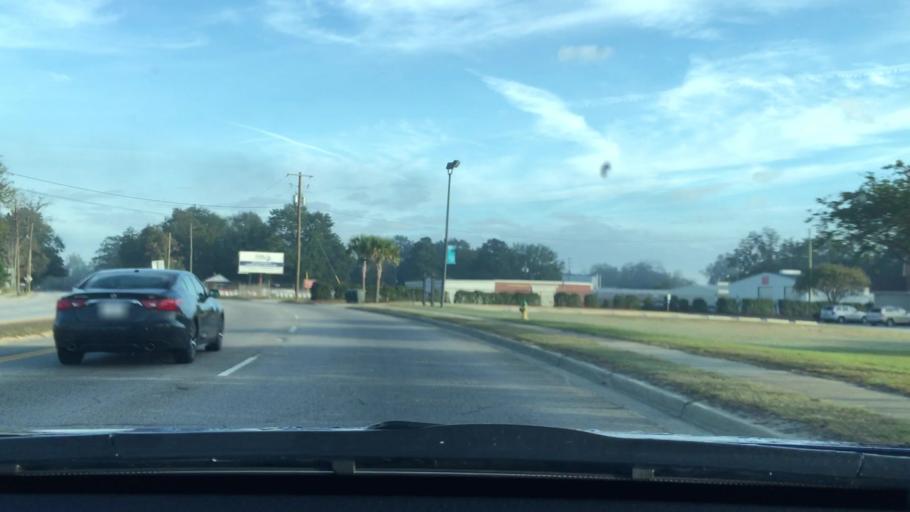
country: US
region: South Carolina
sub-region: Sumter County
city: South Sumter
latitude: 33.8976
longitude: -80.3367
